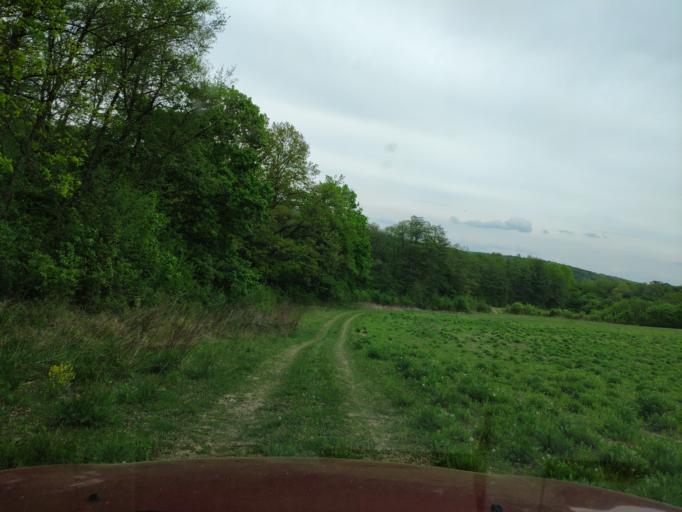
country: SK
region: Banskobystricky
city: Revuca
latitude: 48.5187
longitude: 20.1456
